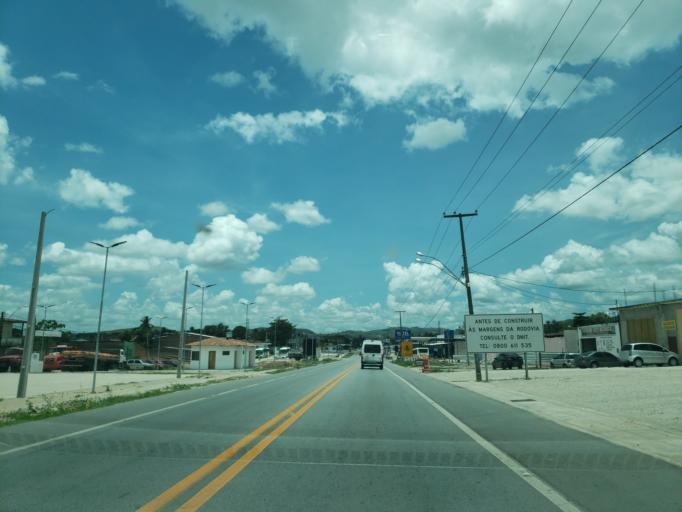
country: BR
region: Alagoas
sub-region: Uniao Dos Palmares
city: Uniao dos Palmares
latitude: -9.1642
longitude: -36.0191
